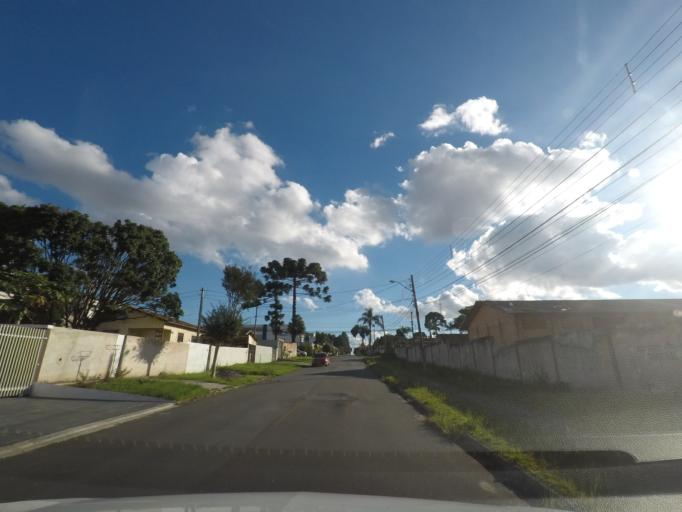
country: BR
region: Parana
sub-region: Curitiba
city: Curitiba
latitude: -25.4806
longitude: -49.2566
